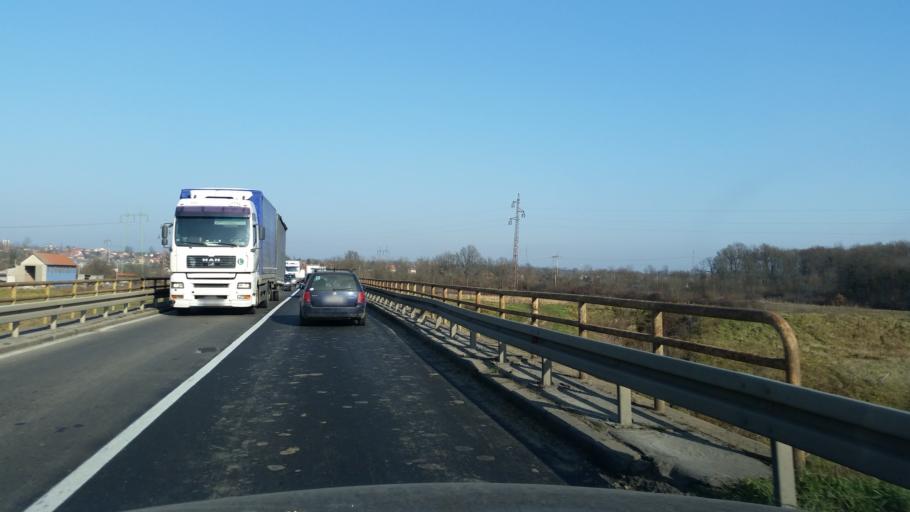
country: RS
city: Stepojevac
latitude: 44.4949
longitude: 20.2849
